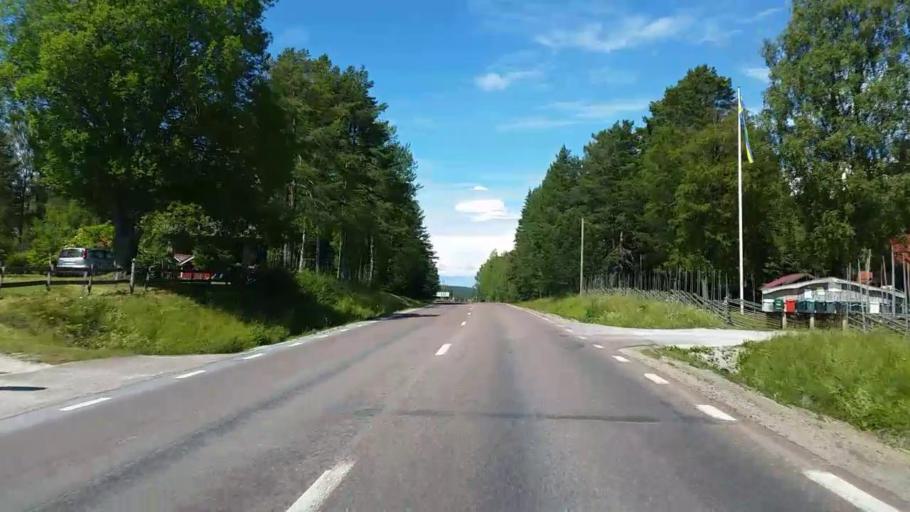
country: SE
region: Dalarna
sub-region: Rattviks Kommun
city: Raettvik
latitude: 61.0352
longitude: 15.2028
